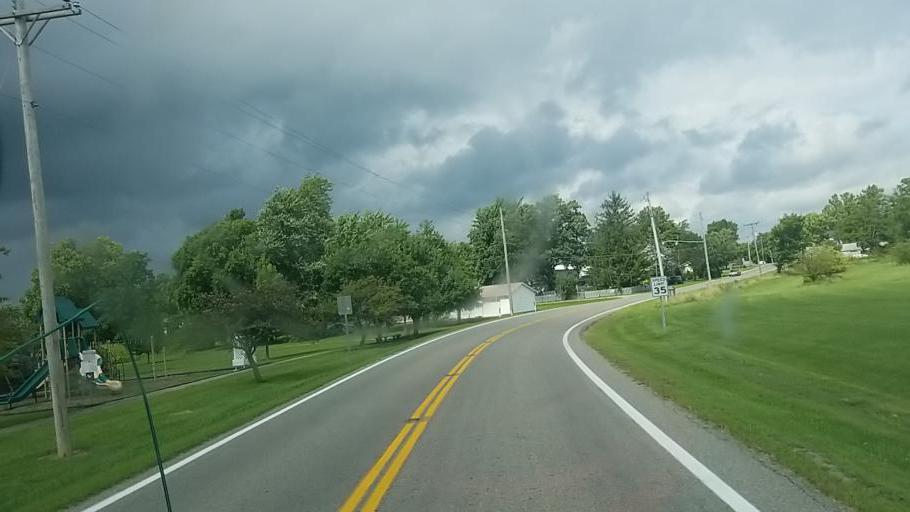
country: US
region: Ohio
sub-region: Champaign County
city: North Lewisburg
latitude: 40.2910
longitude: -83.5838
